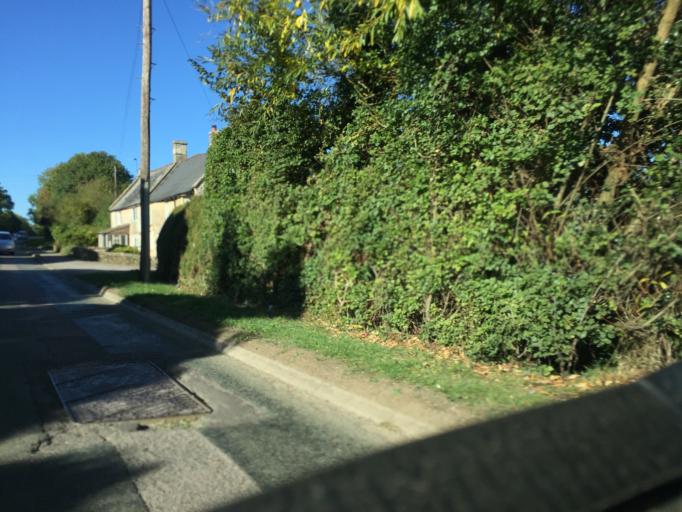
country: GB
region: England
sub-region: Wiltshire
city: Biddestone
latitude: 51.4719
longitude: -2.1930
